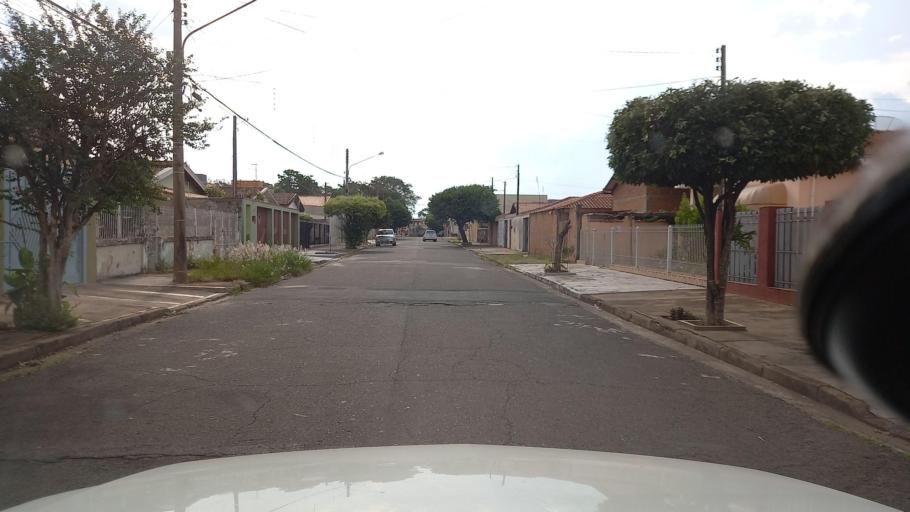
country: BR
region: Sao Paulo
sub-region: Moji-Guacu
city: Mogi-Gaucu
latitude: -22.3490
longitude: -46.9436
